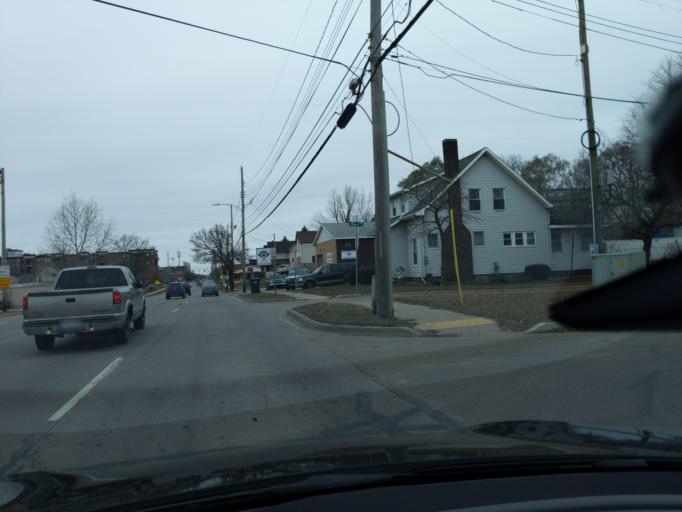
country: US
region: Michigan
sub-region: Ingham County
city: Lansing
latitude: 42.7308
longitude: -84.5447
